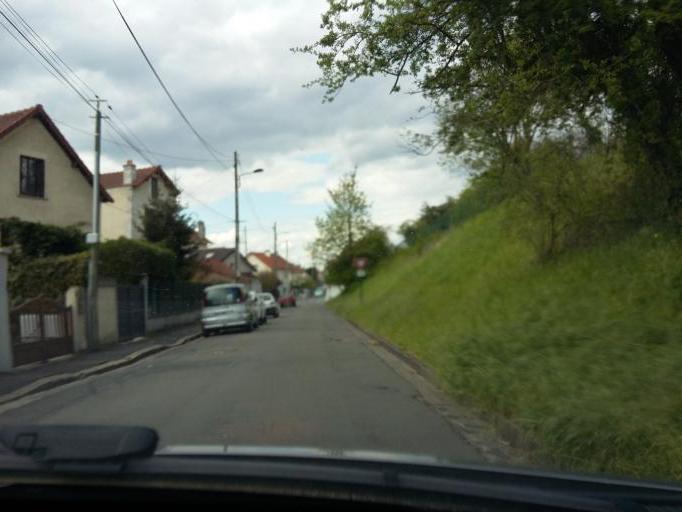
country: FR
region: Ile-de-France
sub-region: Departement du Val-d'Oise
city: Ermont
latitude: 48.9759
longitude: 2.2625
